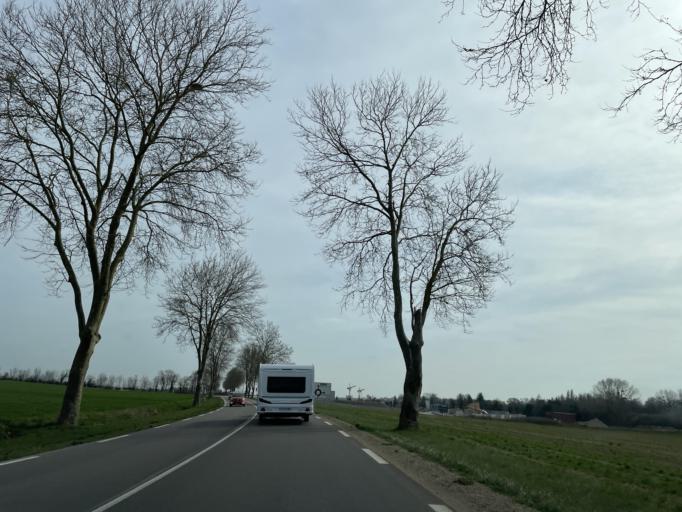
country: FR
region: Champagne-Ardenne
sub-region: Departement de l'Aube
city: Romilly-sur-Seine
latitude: 48.5078
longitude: 3.6938
